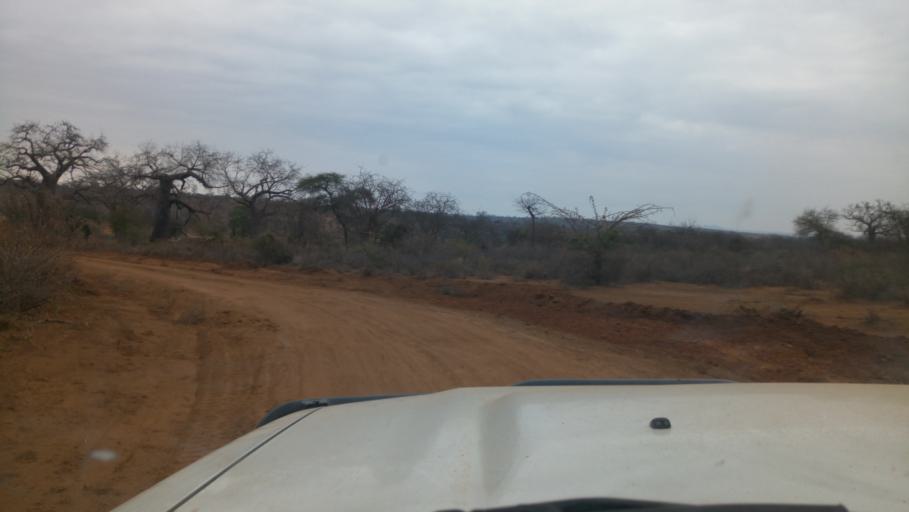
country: KE
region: Makueni
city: Wote
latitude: -1.9215
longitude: 38.1227
